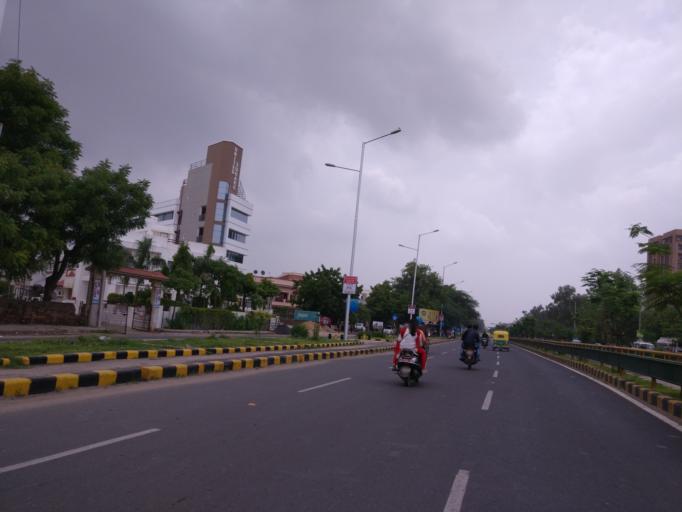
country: IN
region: Gujarat
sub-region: Gandhinagar
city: Adalaj
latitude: 23.1119
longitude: 72.5841
